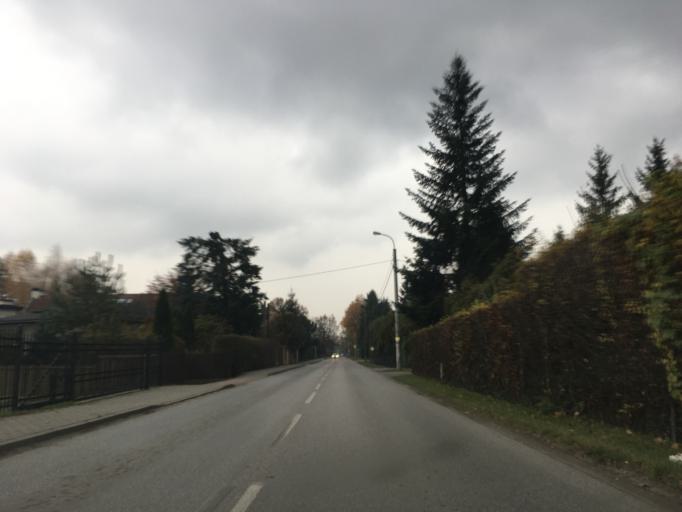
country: PL
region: Masovian Voivodeship
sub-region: Powiat piaseczynski
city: Piaseczno
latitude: 52.0533
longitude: 21.0051
